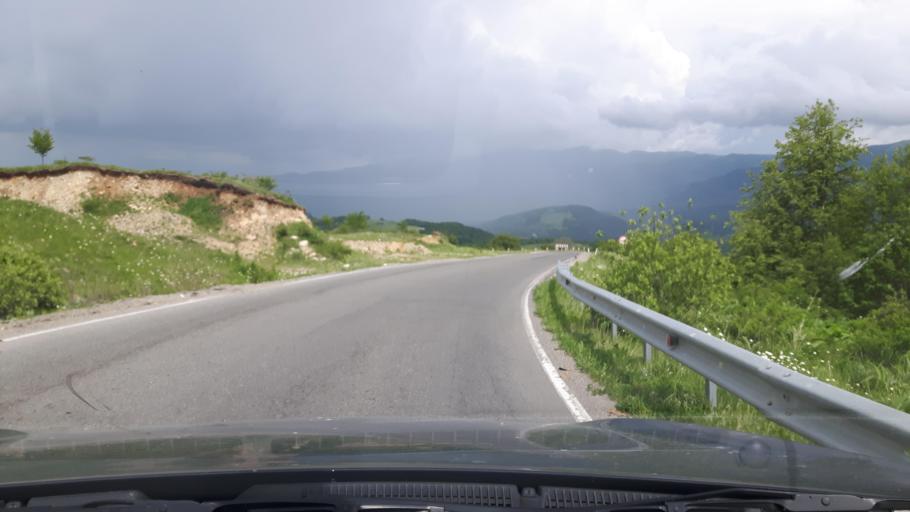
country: GE
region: Kakheti
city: Sagarejo
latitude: 41.8648
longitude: 45.2828
